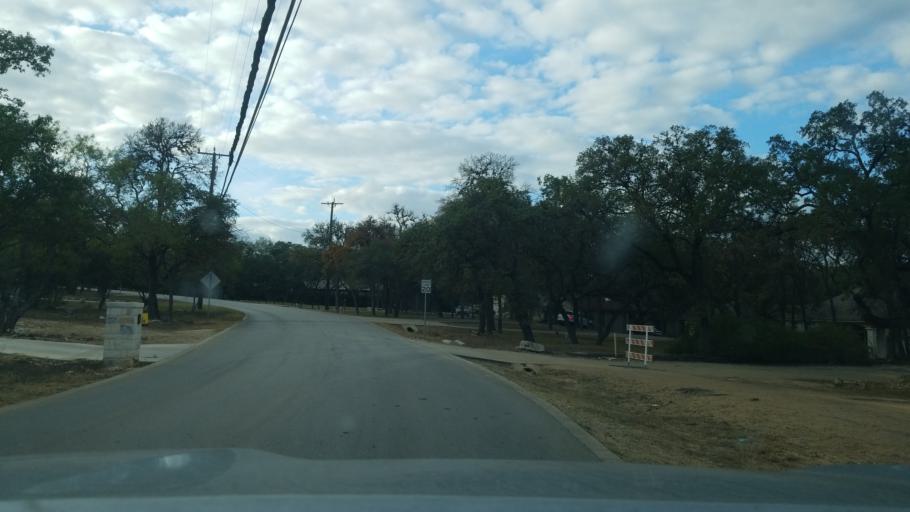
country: US
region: Texas
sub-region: Bexar County
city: Hollywood Park
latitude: 29.5936
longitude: -98.4745
